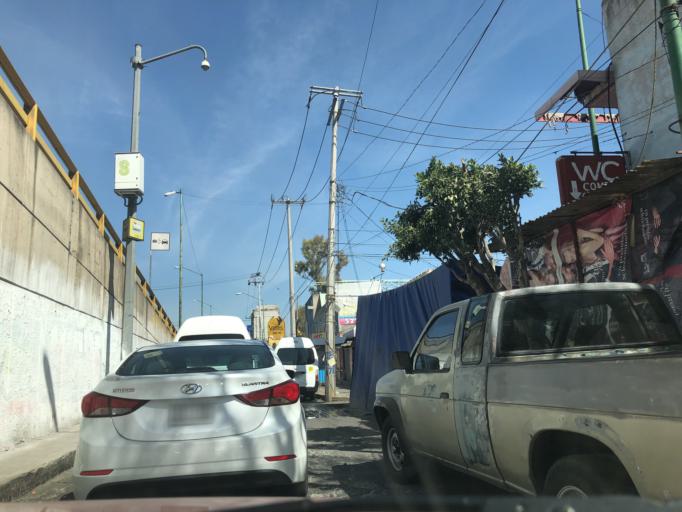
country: MX
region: Mexico
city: Ciudad Nezahualcoyotl
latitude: 19.3869
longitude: -99.0363
